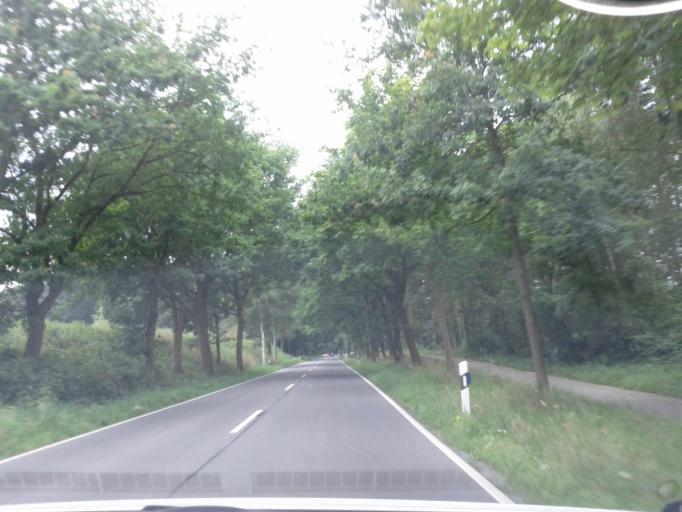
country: DE
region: Lower Saxony
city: Kranenburg
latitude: 53.6295
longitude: 9.2032
